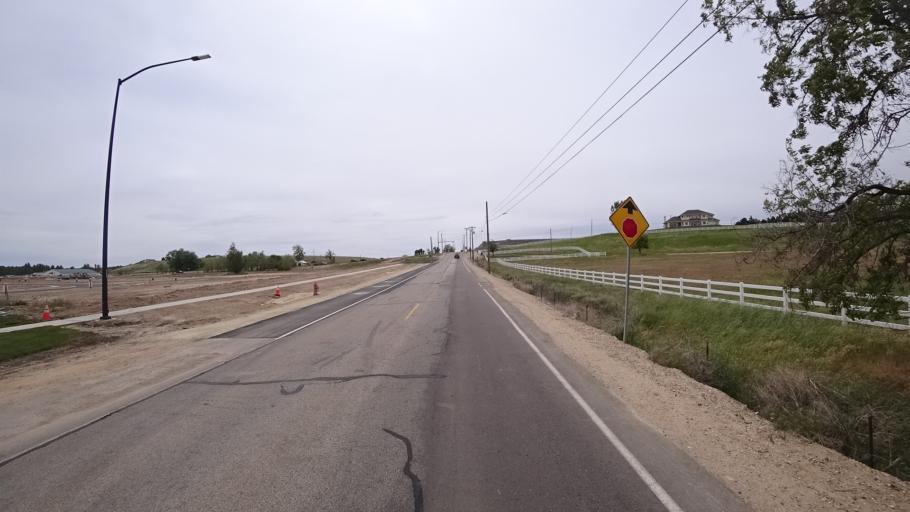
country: US
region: Idaho
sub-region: Ada County
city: Meridian
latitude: 43.5481
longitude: -116.3541
